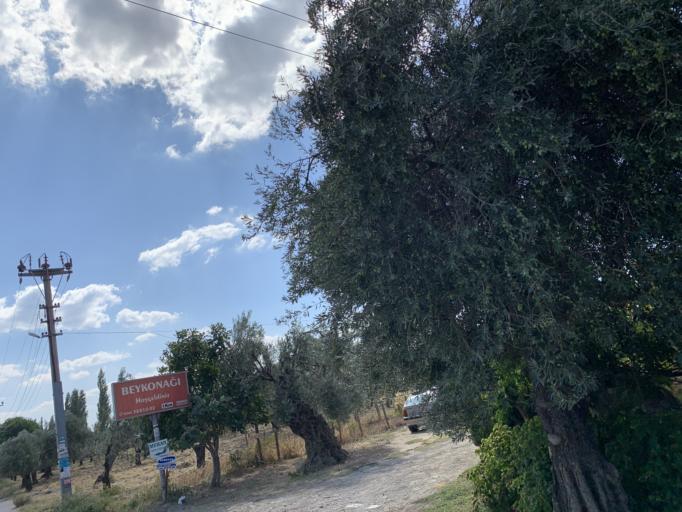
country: TR
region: Balikesir
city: Altinoluk
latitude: 39.5673
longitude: 26.8355
